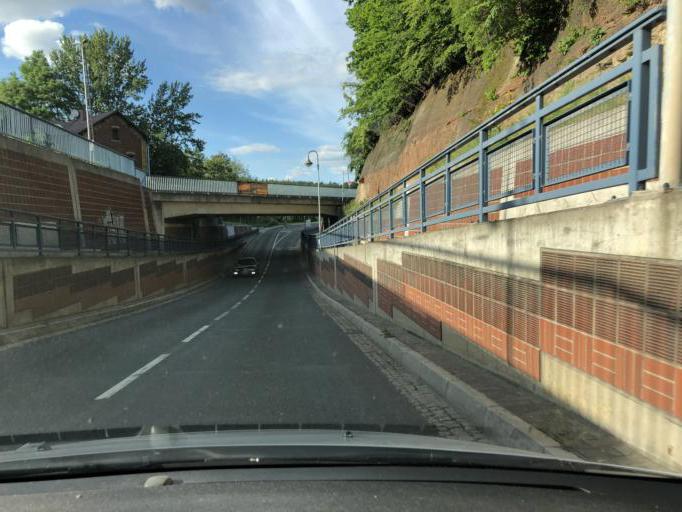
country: DE
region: Thuringia
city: Schmolln
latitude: 50.9004
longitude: 12.3591
